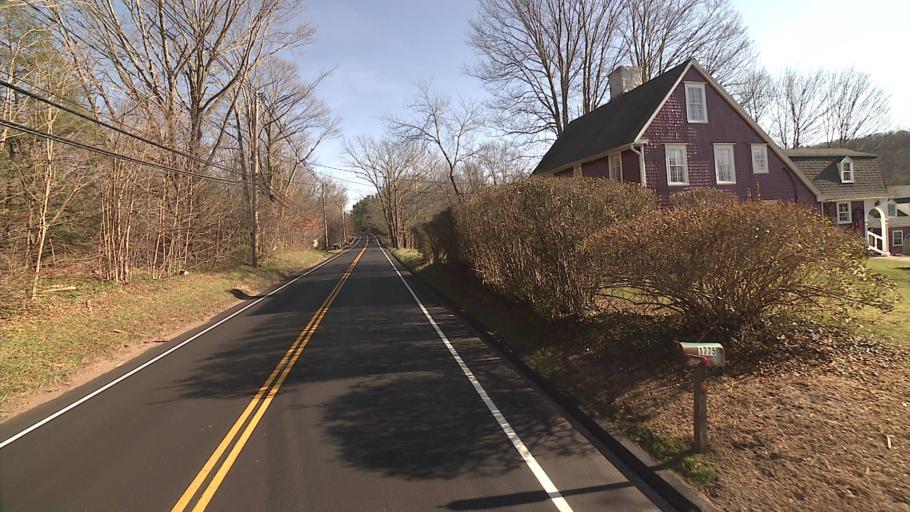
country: US
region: Connecticut
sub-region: New Haven County
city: Wallingford Center
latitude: 41.4093
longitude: -72.7714
